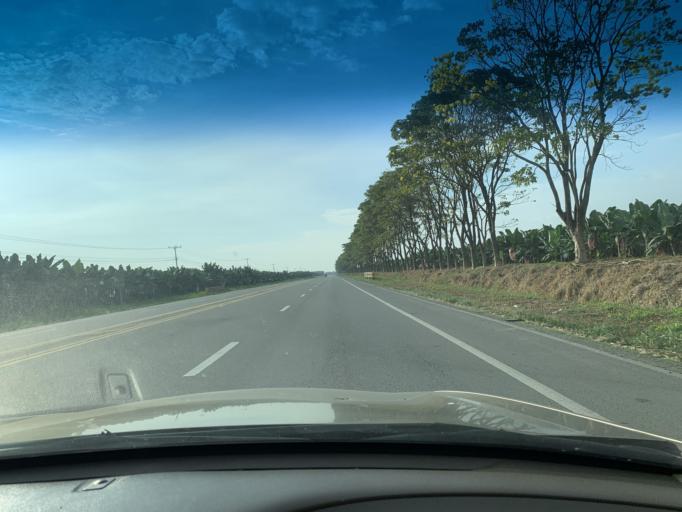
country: EC
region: Guayas
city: Coronel Marcelino Mariduena
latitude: -2.2753
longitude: -79.5351
